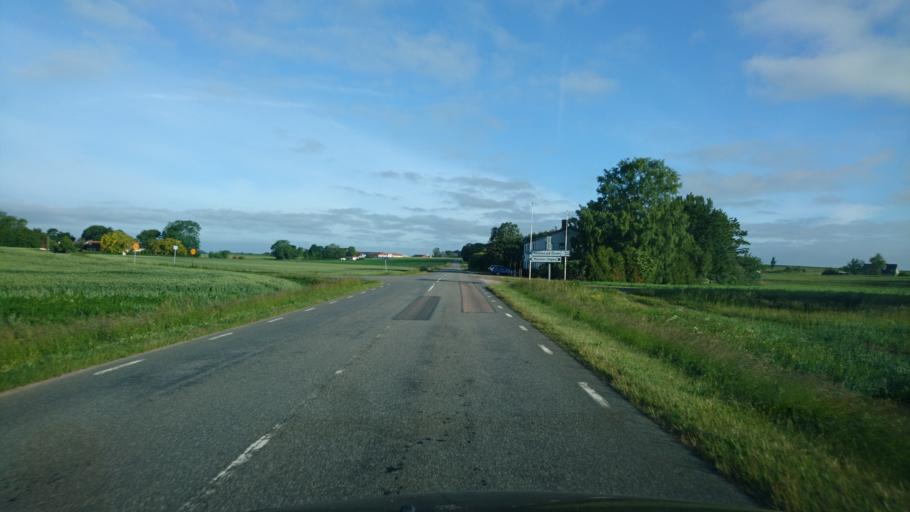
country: SE
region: Skane
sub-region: Tomelilla Kommun
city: Tomelilla
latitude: 55.4595
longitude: 14.1070
